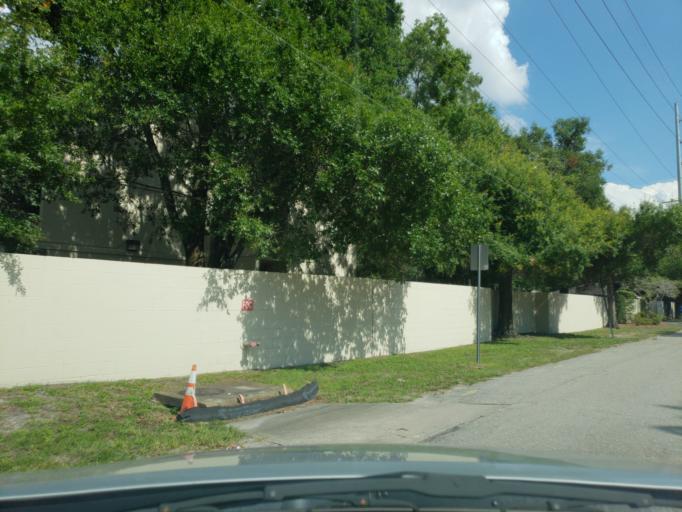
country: US
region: Florida
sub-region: Hillsborough County
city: Egypt Lake-Leto
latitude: 27.9774
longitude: -82.4959
